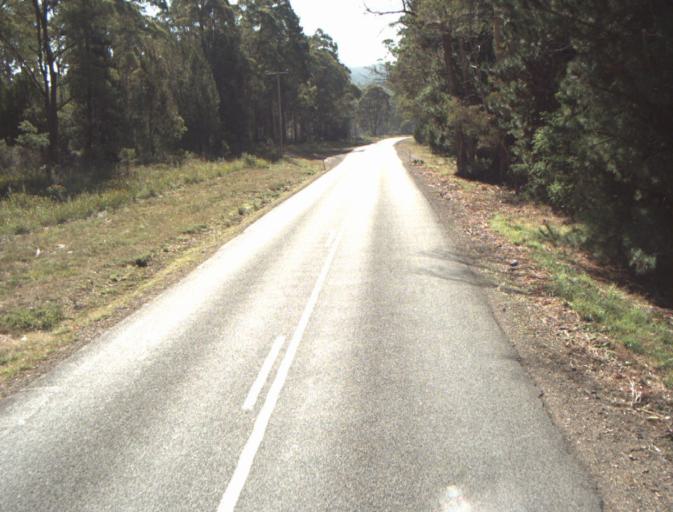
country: AU
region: Tasmania
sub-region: Launceston
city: Mayfield
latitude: -41.2867
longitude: 147.1274
